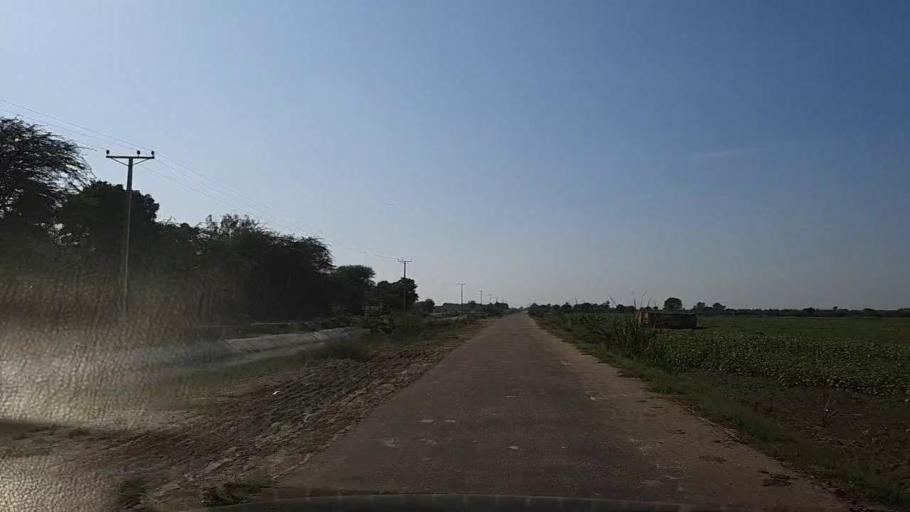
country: PK
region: Sindh
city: Thatta
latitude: 24.5967
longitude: 67.8108
